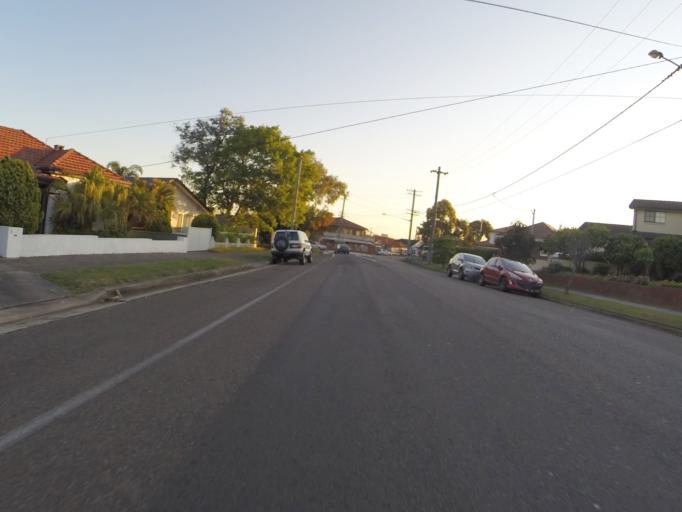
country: AU
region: New South Wales
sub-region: Rockdale
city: Bexley
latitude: -33.9454
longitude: 151.1133
